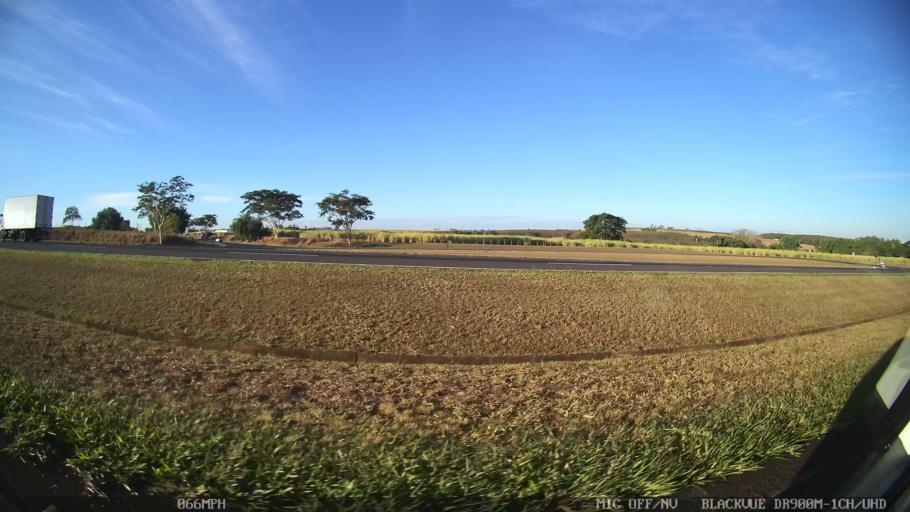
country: BR
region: Sao Paulo
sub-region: Guapiacu
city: Guapiacu
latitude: -20.9339
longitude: -49.2697
